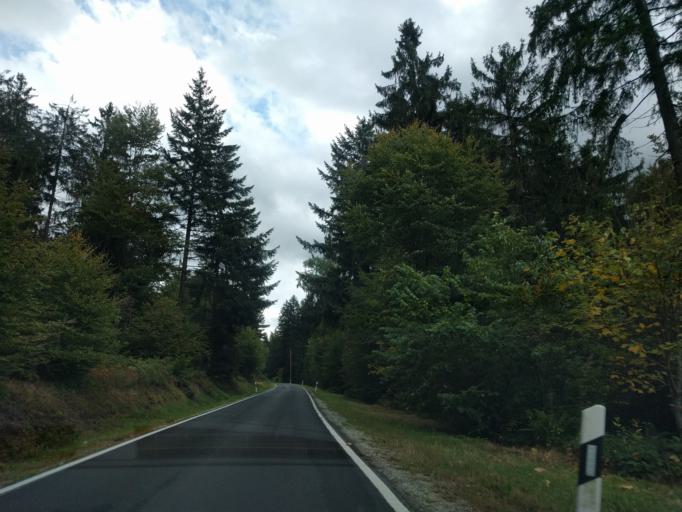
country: DE
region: Bavaria
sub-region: Lower Bavaria
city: Grafling
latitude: 48.8770
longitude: 13.0197
